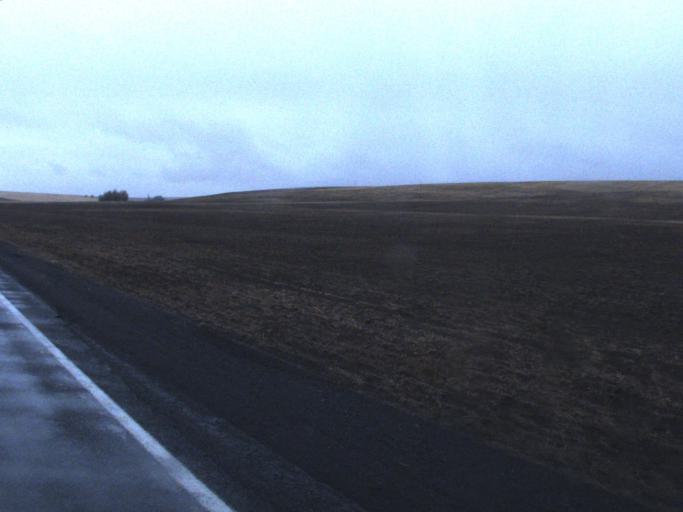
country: US
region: Washington
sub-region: Lincoln County
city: Davenport
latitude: 47.3952
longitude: -118.1525
